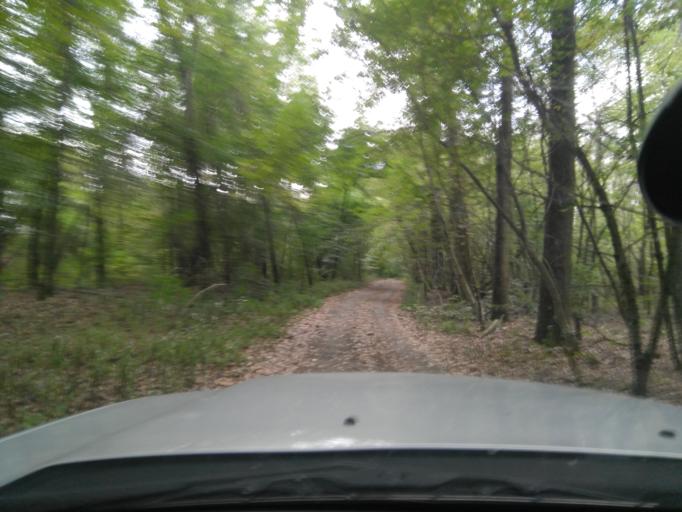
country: HU
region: Bacs-Kiskun
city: Apostag
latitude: 46.8960
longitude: 18.9480
